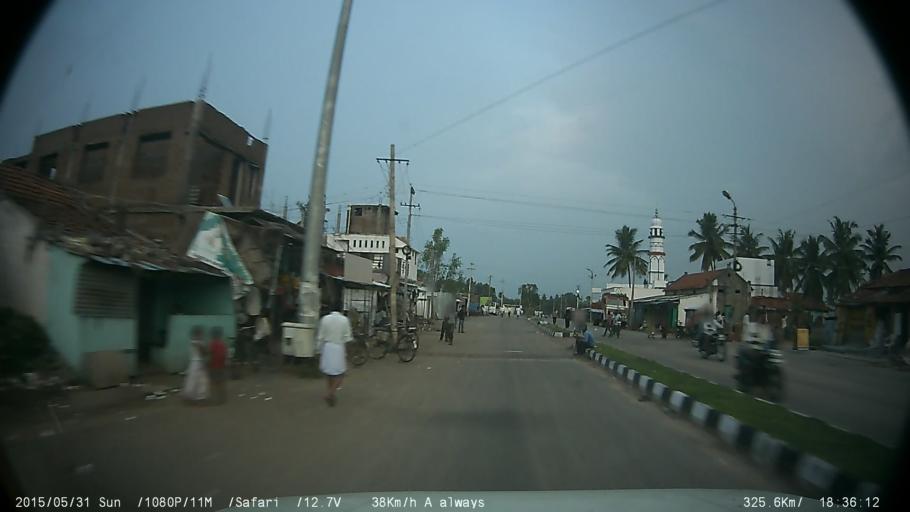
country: IN
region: Karnataka
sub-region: Mysore
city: Nanjangud
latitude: 12.1465
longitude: 76.7646
